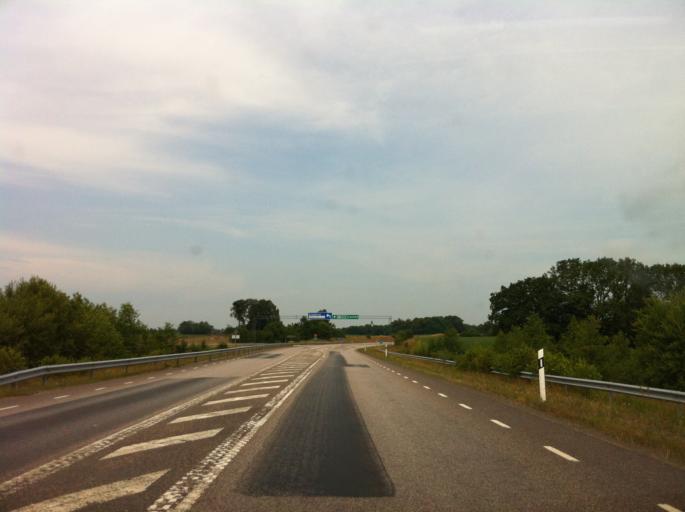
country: SE
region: Kalmar
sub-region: Torsas Kommun
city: Torsas
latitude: 56.4313
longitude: 16.0777
